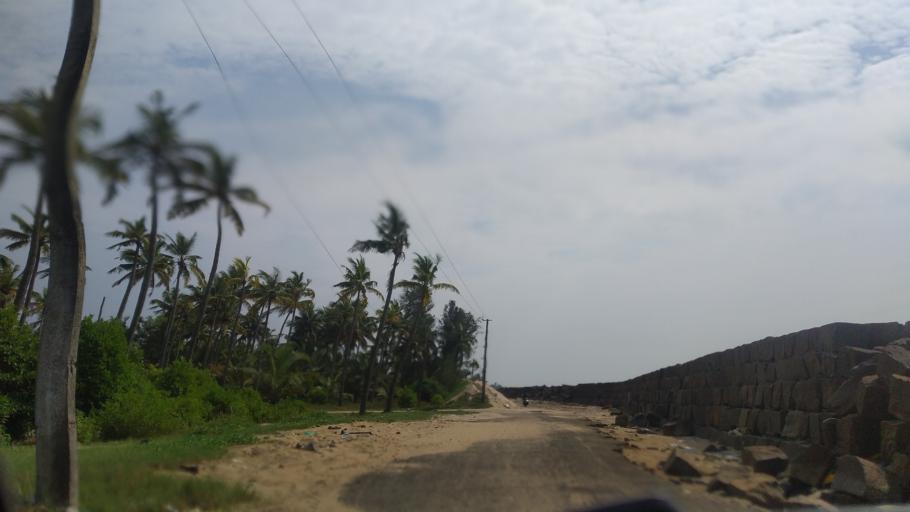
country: IN
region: Kerala
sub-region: Ernakulam
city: Elur
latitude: 10.0870
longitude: 76.1927
